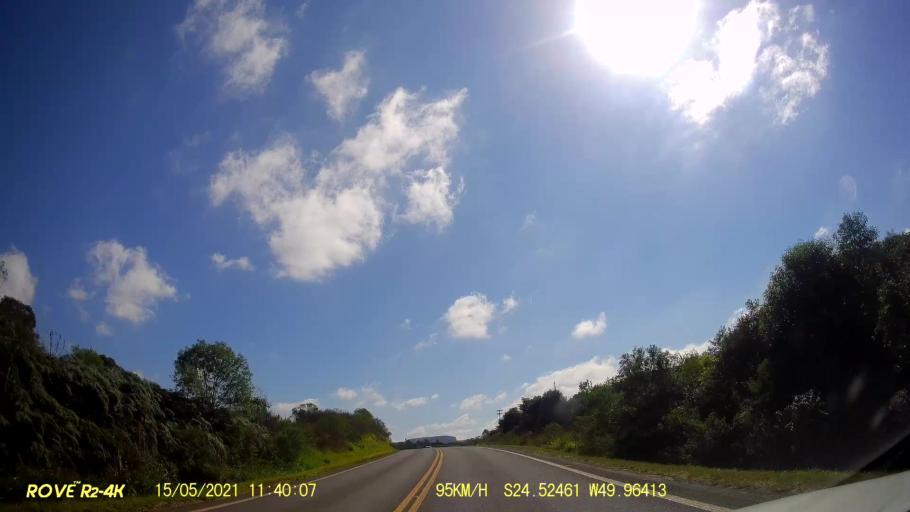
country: BR
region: Parana
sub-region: Pirai Do Sul
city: Pirai do Sul
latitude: -24.5254
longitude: -49.9638
